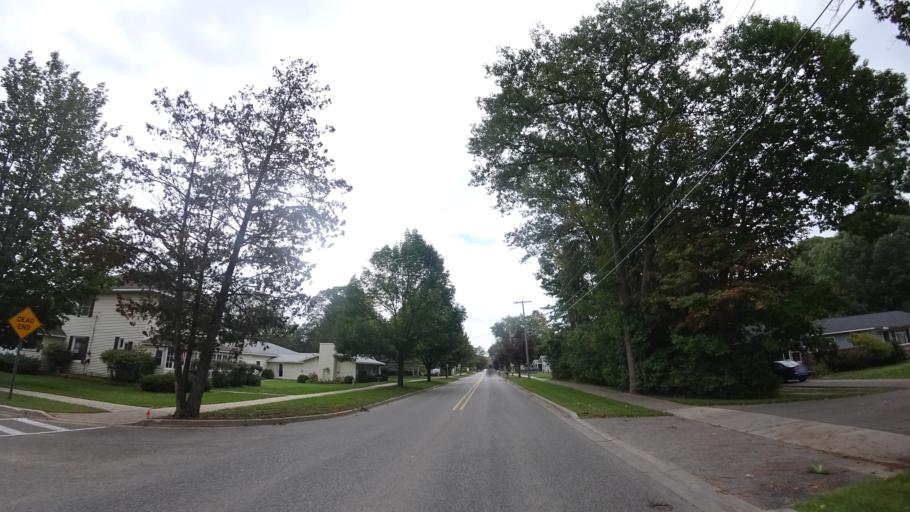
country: US
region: Michigan
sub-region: Emmet County
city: Harbor Springs
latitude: 45.4354
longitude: -84.9810
